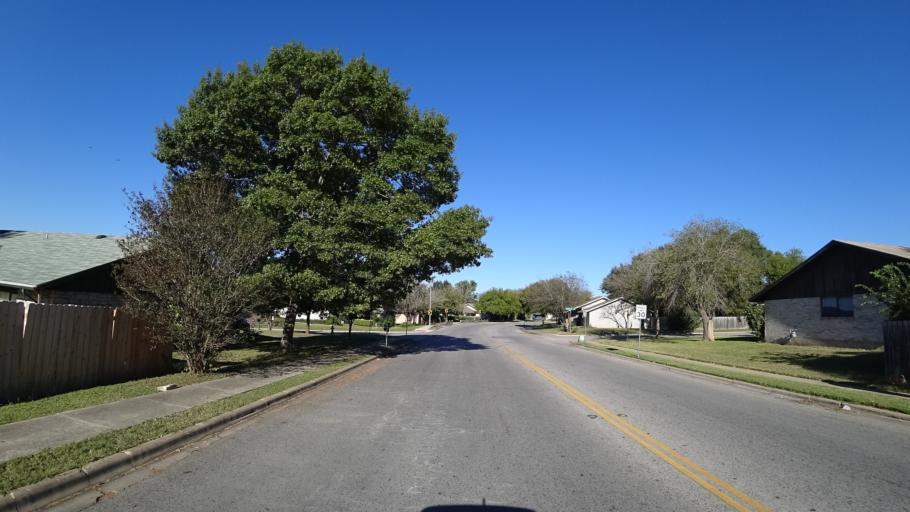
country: US
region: Texas
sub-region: Travis County
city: Austin
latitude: 30.3048
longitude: -97.6642
